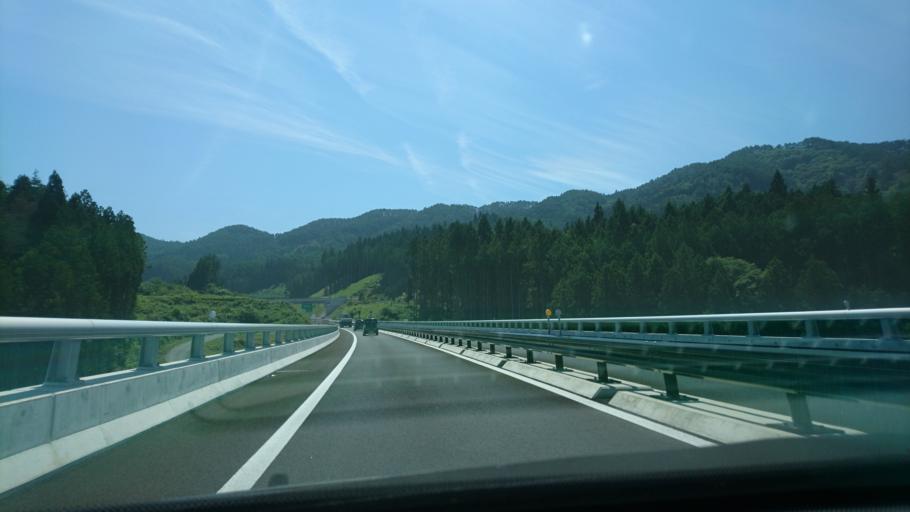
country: JP
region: Iwate
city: Ofunato
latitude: 38.9906
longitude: 141.6126
